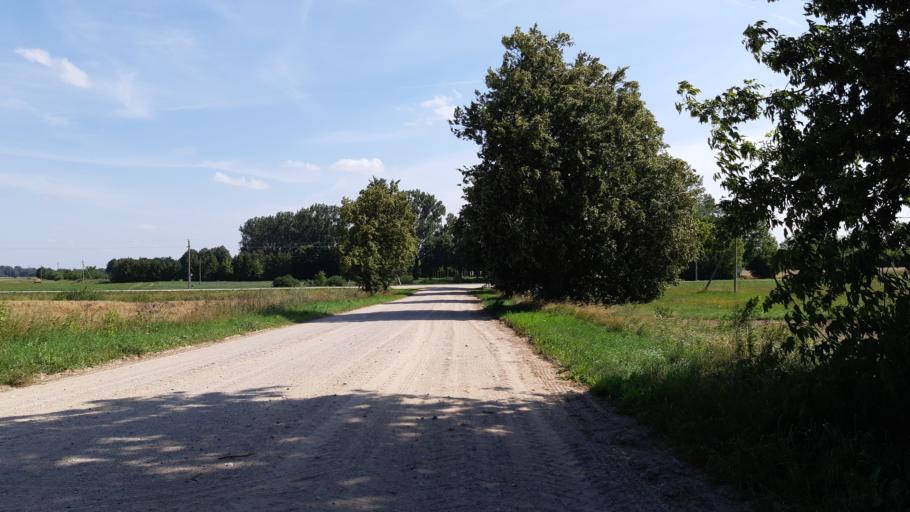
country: LT
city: Virbalis
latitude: 54.6345
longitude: 22.8262
